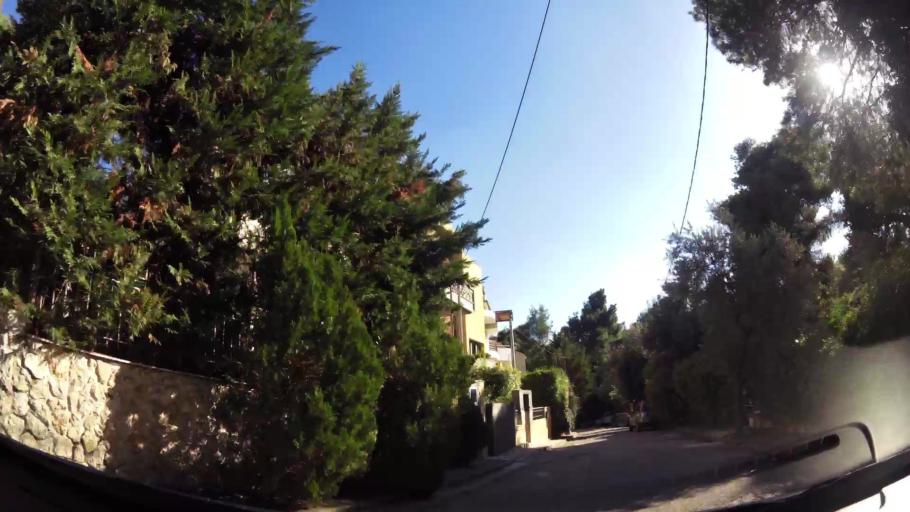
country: GR
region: Attica
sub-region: Nomarchia Athinas
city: Ekali
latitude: 38.1172
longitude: 23.8422
